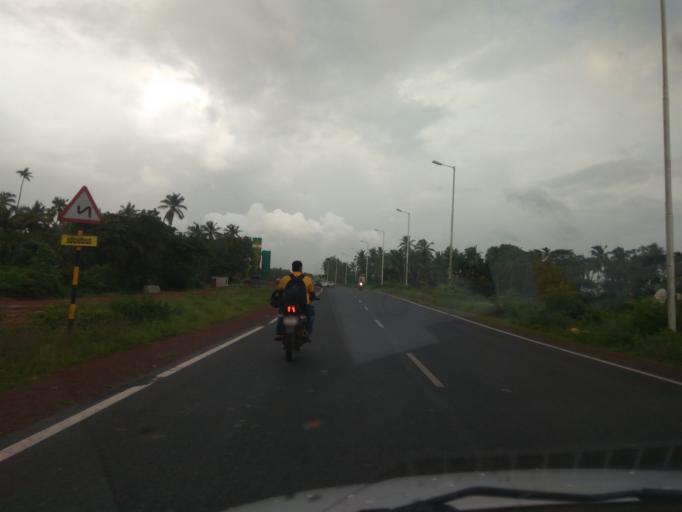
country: IN
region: Goa
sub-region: North Goa
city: Goa Velha
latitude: 15.4341
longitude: 73.8852
